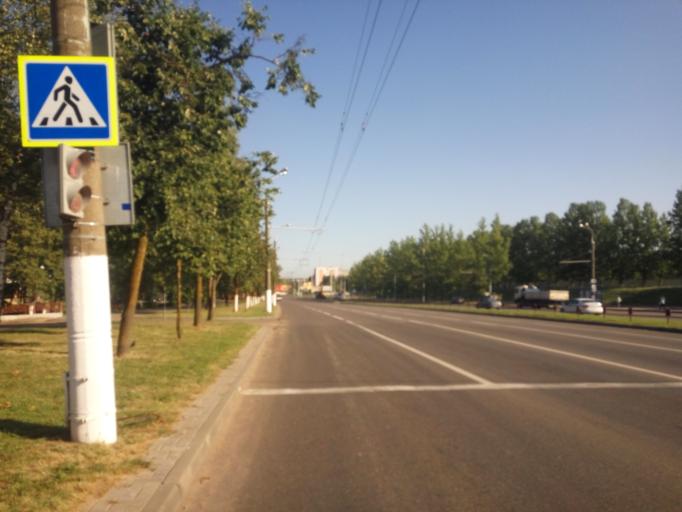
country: BY
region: Vitebsk
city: Vitebsk
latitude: 55.1929
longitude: 30.2496
